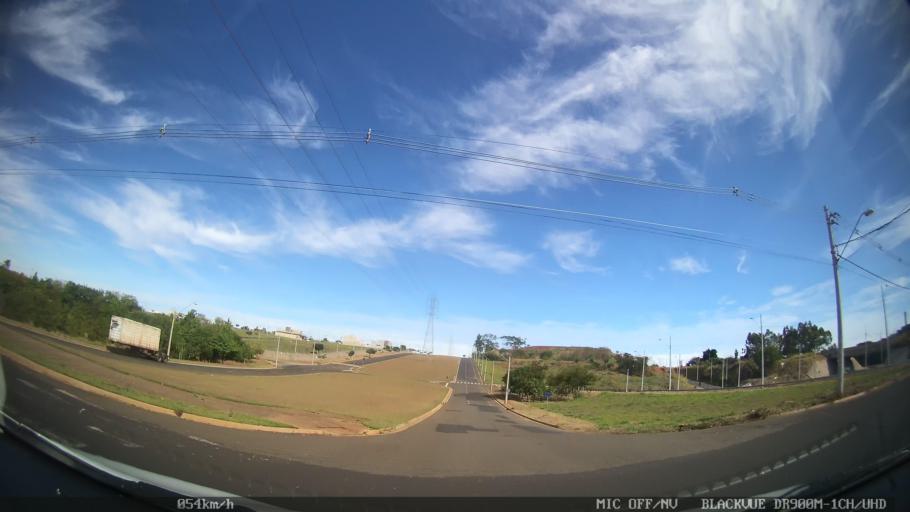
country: BR
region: Sao Paulo
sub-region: Sao Jose Do Rio Preto
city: Sao Jose do Rio Preto
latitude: -20.8478
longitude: -49.3734
